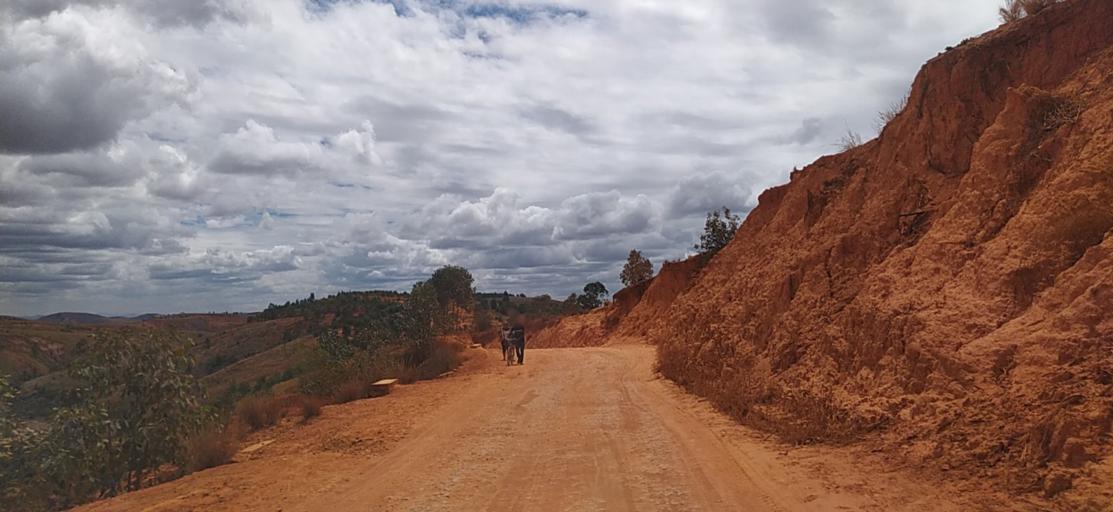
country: MG
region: Alaotra Mangoro
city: Ambatondrazaka
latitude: -18.0603
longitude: 48.2568
